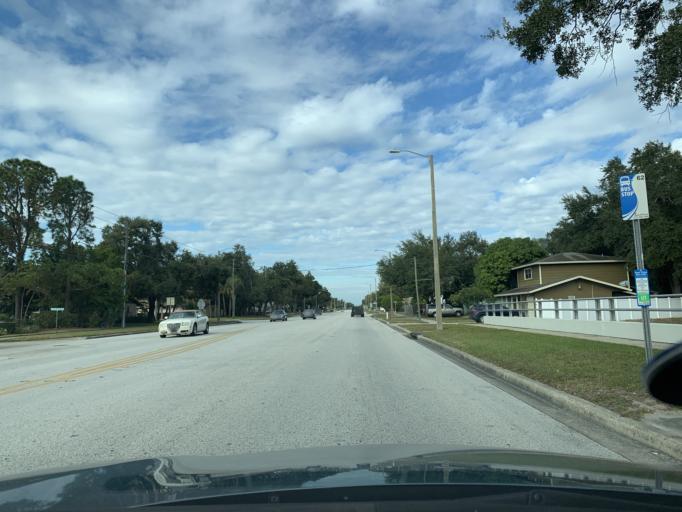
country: US
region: Florida
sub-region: Pinellas County
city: Kenneth City
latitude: 27.8220
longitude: -82.7367
